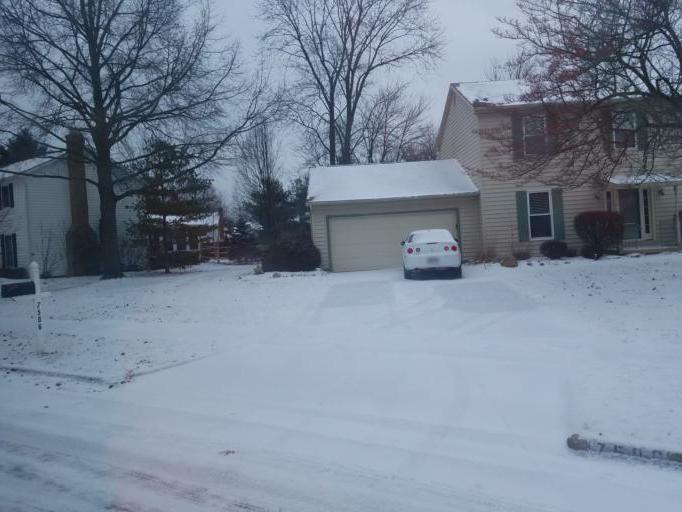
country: US
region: Ohio
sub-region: Franklin County
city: Dublin
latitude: 40.1136
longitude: -83.0730
